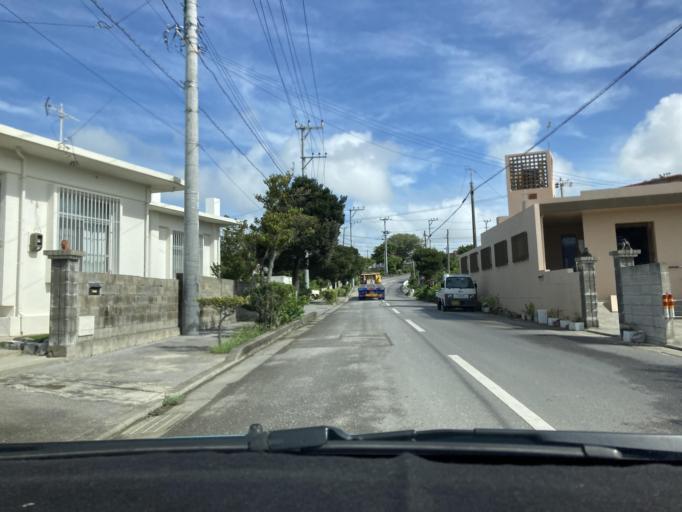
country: JP
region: Okinawa
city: Itoman
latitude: 26.1044
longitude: 127.6626
